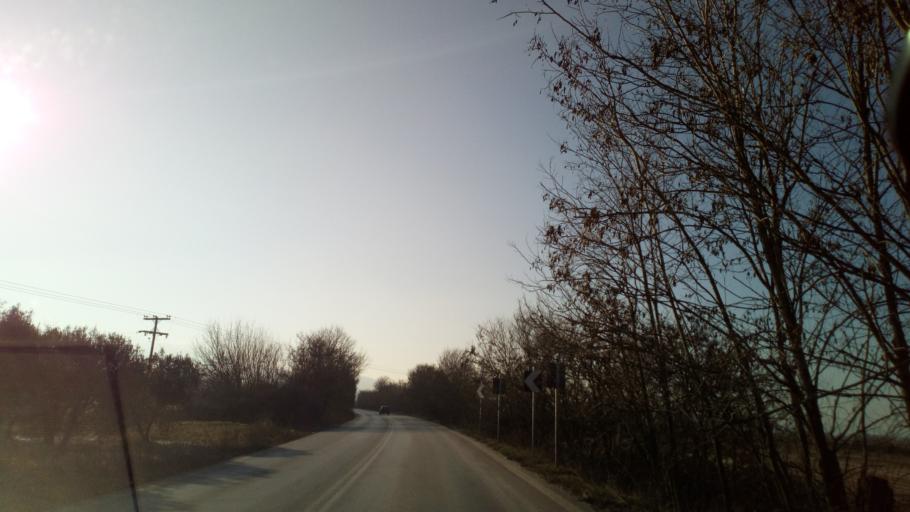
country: GR
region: Central Macedonia
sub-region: Nomos Thessalonikis
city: Gerakarou
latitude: 40.6330
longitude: 23.2290
